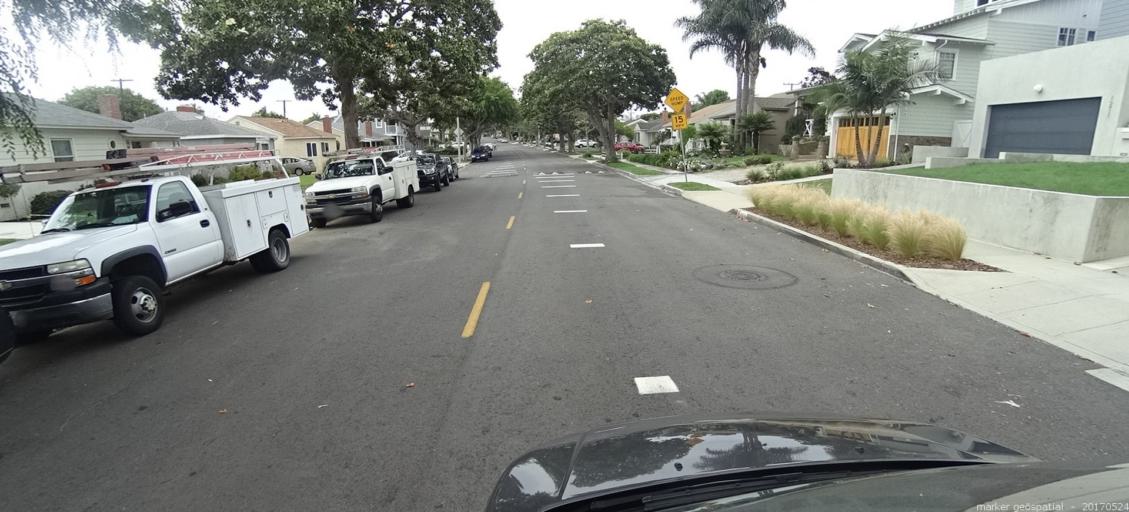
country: US
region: California
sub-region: Los Angeles County
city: Palos Verdes Estates
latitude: 33.8239
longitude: -118.3832
